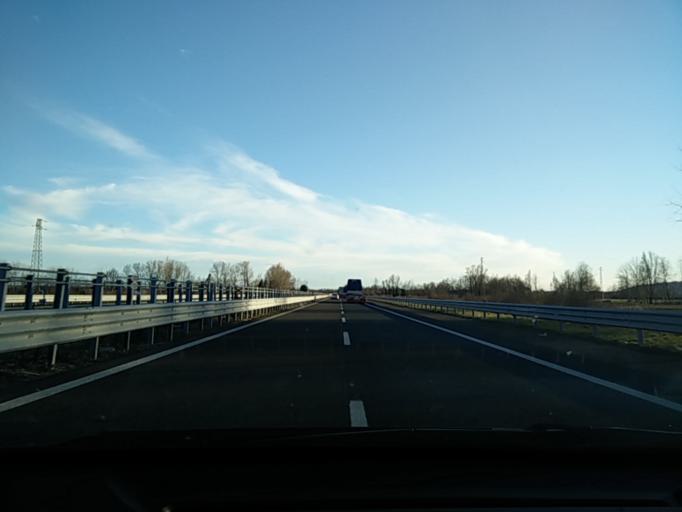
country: IT
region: Friuli Venezia Giulia
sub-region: Provincia di Udine
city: Buia
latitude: 46.2274
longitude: 13.0945
